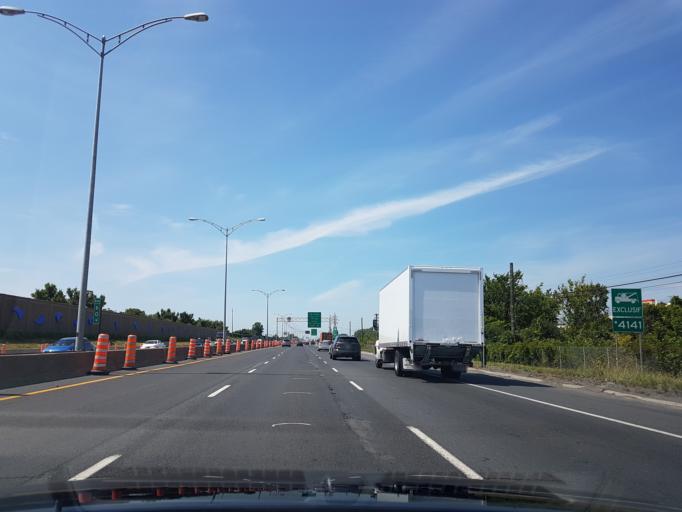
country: CA
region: Quebec
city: Cote-Saint-Luc
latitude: 45.4474
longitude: -73.6802
